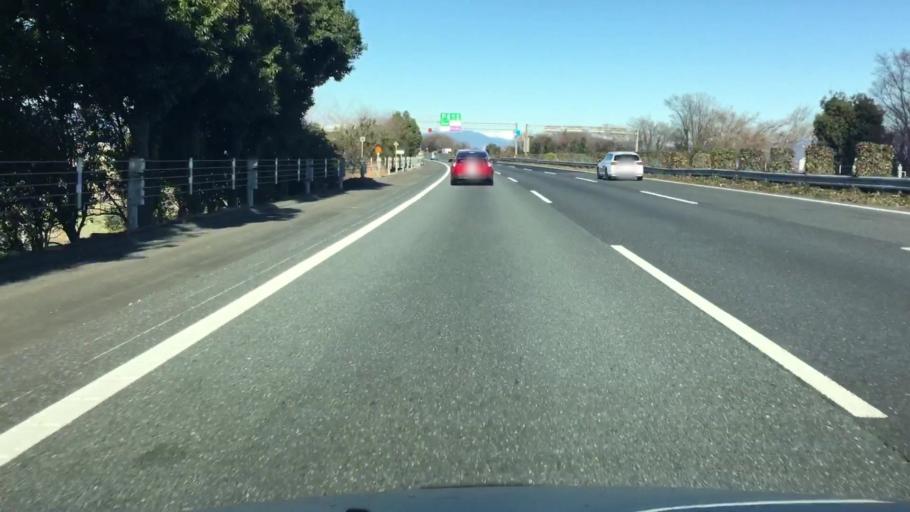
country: JP
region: Saitama
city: Honjo
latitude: 36.2415
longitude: 139.1447
